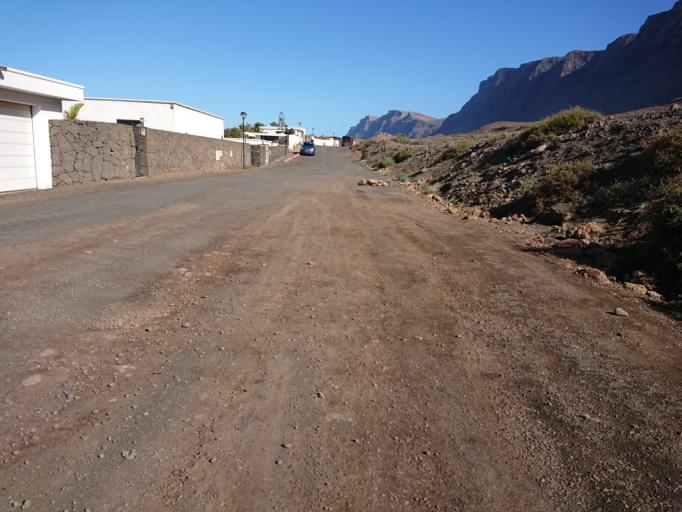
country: ES
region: Canary Islands
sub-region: Provincia de Las Palmas
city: Teguise
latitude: 29.1124
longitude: -13.5450
